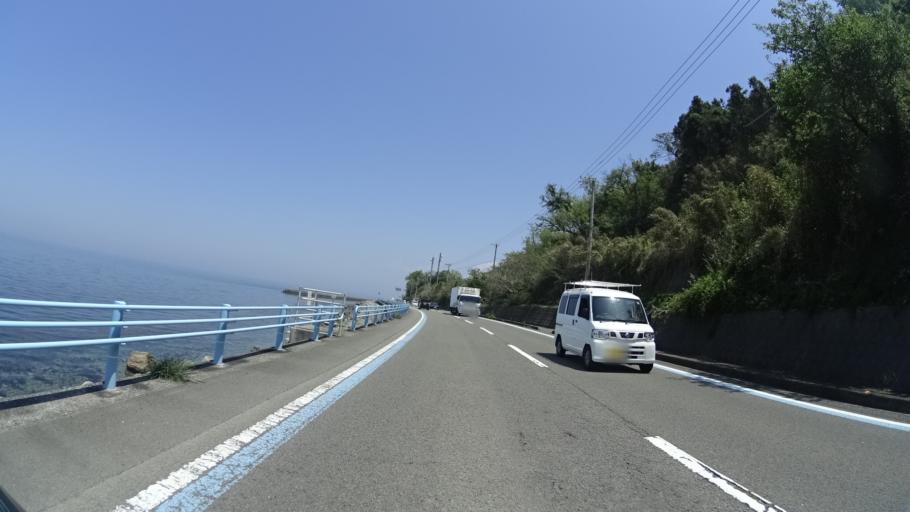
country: JP
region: Ehime
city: Iyo
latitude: 33.6753
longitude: 132.6166
